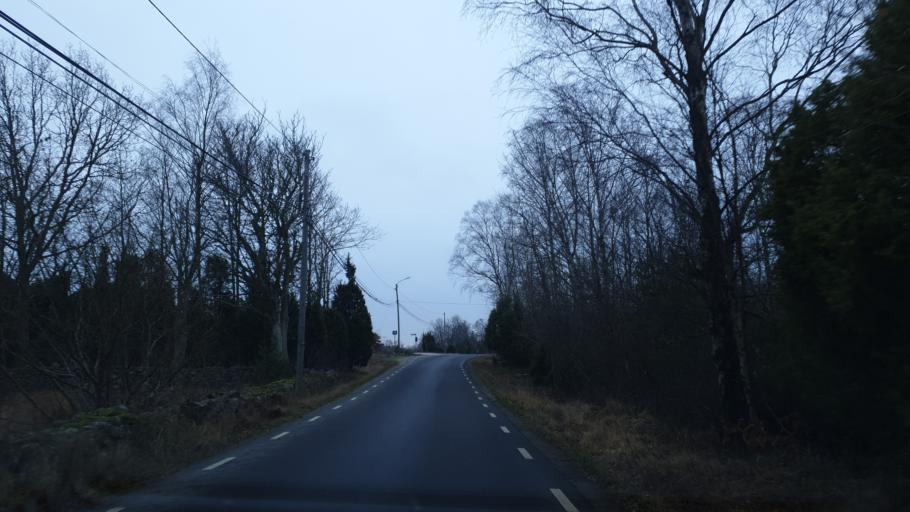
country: SE
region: Blekinge
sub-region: Karlskrona Kommun
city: Karlskrona
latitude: 56.1138
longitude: 15.6135
